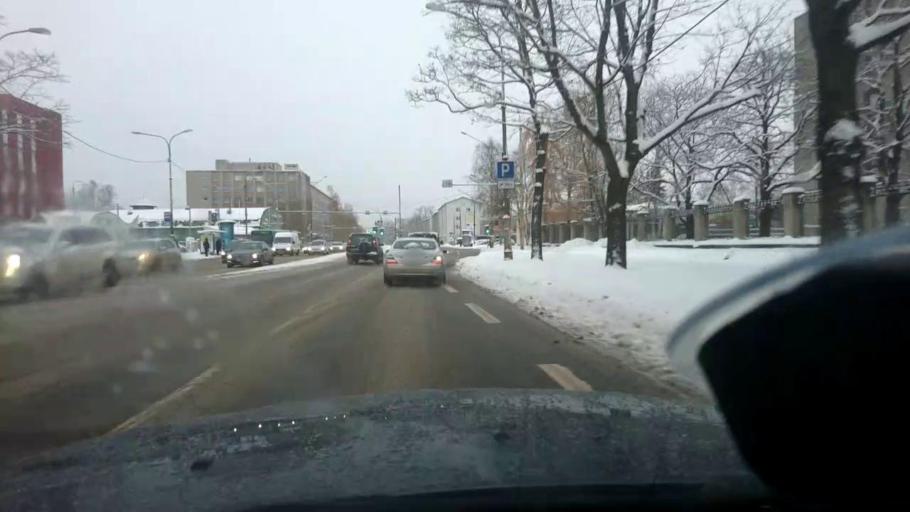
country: EE
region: Harju
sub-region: Tallinna linn
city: Tallinn
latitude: 59.4087
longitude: 24.7355
